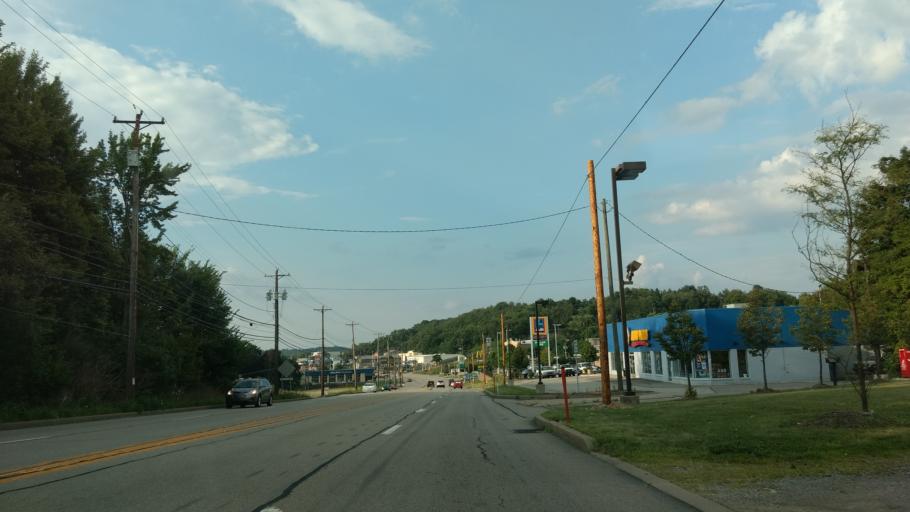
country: US
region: Pennsylvania
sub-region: Allegheny County
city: Allison Park
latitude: 40.5878
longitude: -79.9498
